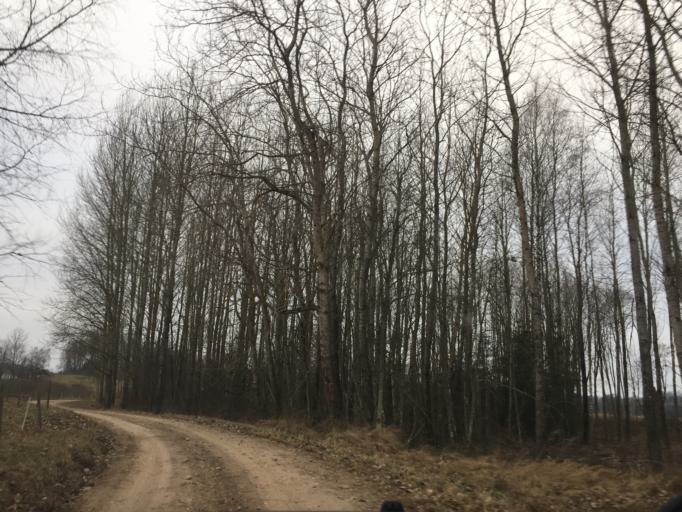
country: LV
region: Ligatne
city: Ligatne
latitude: 57.2254
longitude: 25.1278
